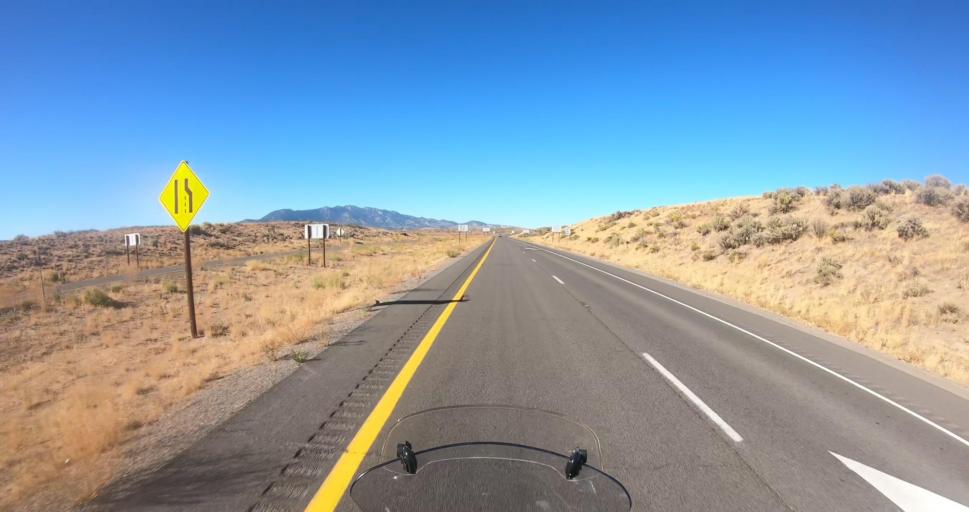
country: US
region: Nevada
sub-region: Washoe County
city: Cold Springs
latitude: 39.7820
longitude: -120.0385
